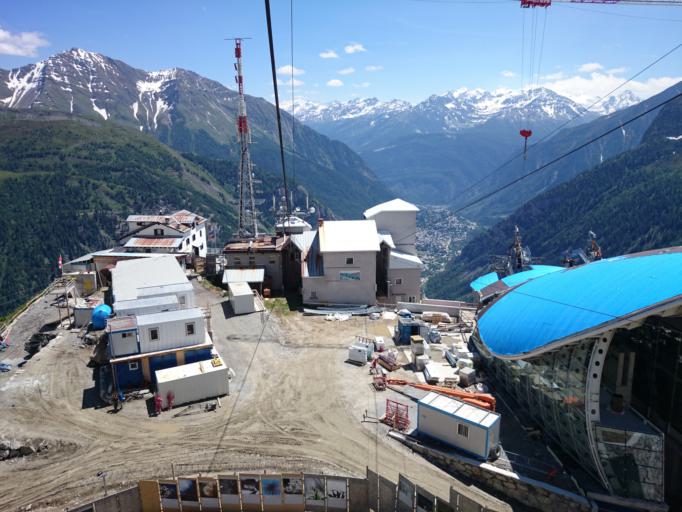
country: IT
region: Aosta Valley
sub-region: Valle d'Aosta
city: Courmayeur
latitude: 45.8298
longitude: 6.9497
